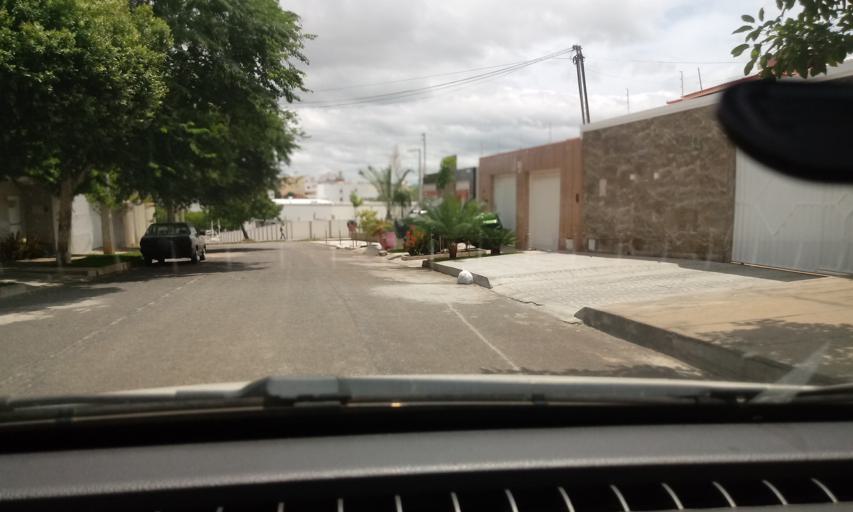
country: BR
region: Bahia
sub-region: Guanambi
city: Guanambi
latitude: -14.2284
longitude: -42.7756
